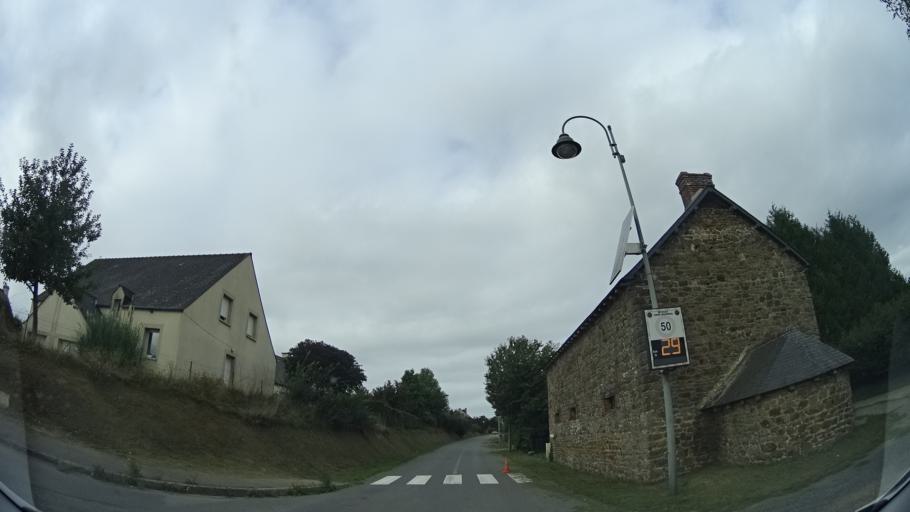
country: FR
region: Brittany
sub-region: Departement d'Ille-et-Vilaine
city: Irodouer
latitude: 48.2858
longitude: -1.9273
